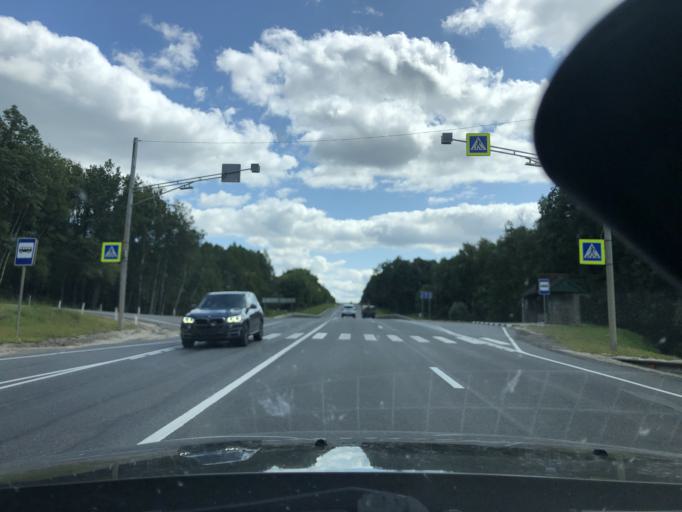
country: RU
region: Tula
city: Gorelki
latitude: 54.3210
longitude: 37.5601
